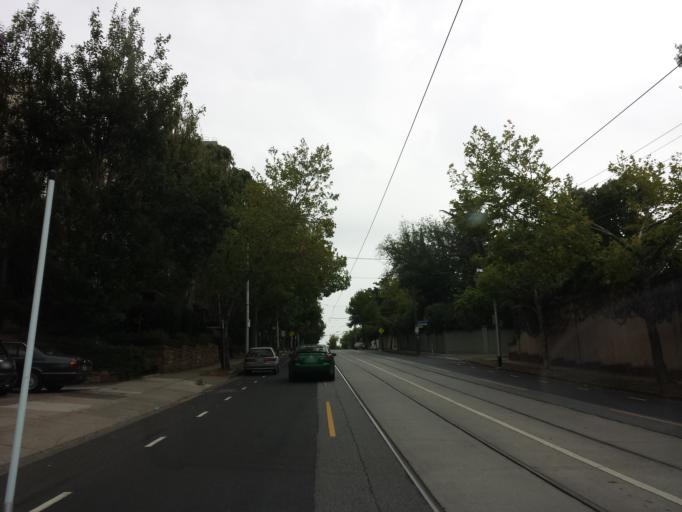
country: AU
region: Victoria
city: Toorak
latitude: -37.8426
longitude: 145.0217
